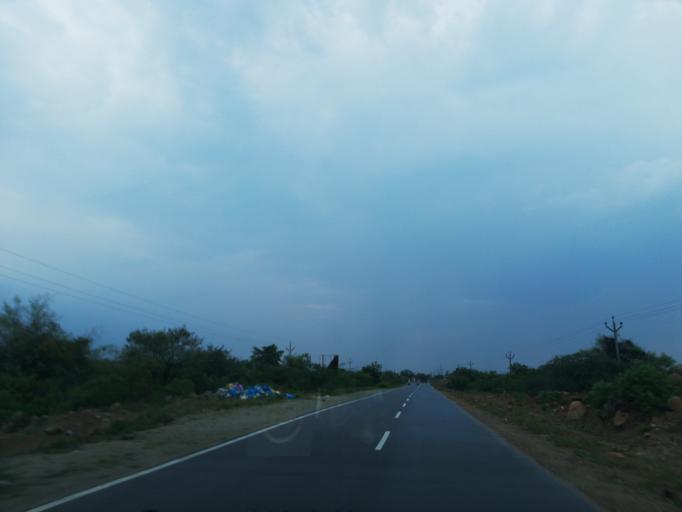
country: IN
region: Andhra Pradesh
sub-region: Guntur
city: Macherla
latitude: 16.6681
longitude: 79.2816
